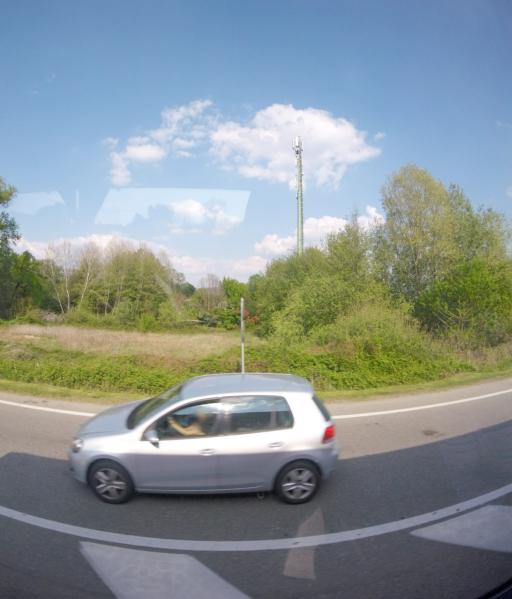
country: IT
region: Piedmont
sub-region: Provincia di Novara
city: Dormelletto
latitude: 45.7364
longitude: 8.5725
